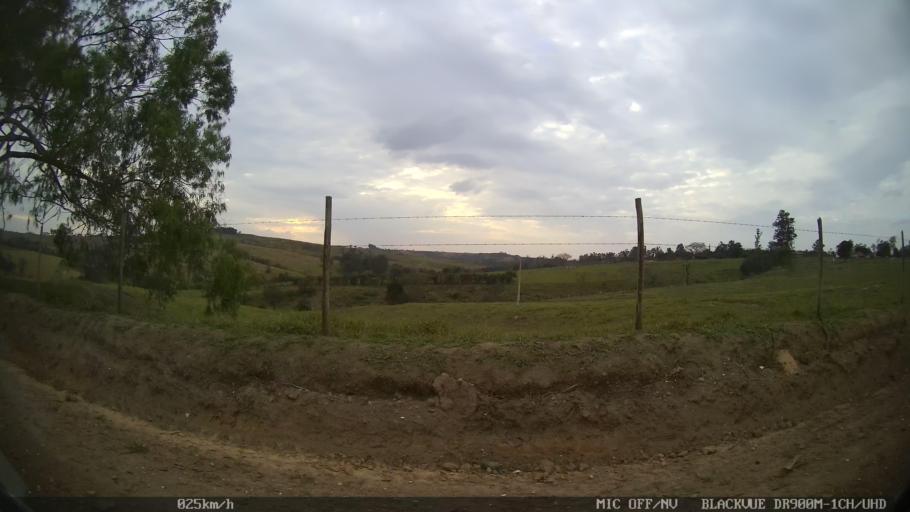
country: BR
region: Sao Paulo
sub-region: Americana
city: Americana
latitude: -22.6791
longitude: -47.3758
